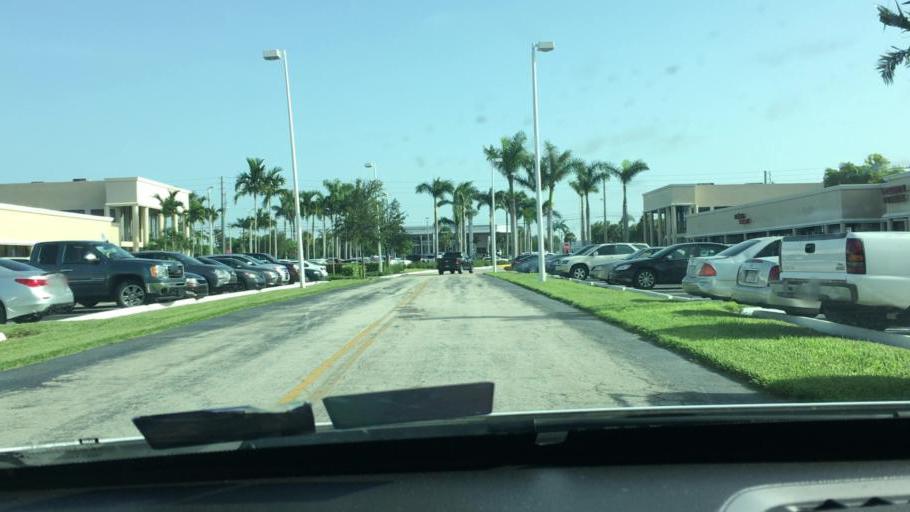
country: US
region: Florida
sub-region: Palm Beach County
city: Schall Circle
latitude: 26.7083
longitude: -80.1033
